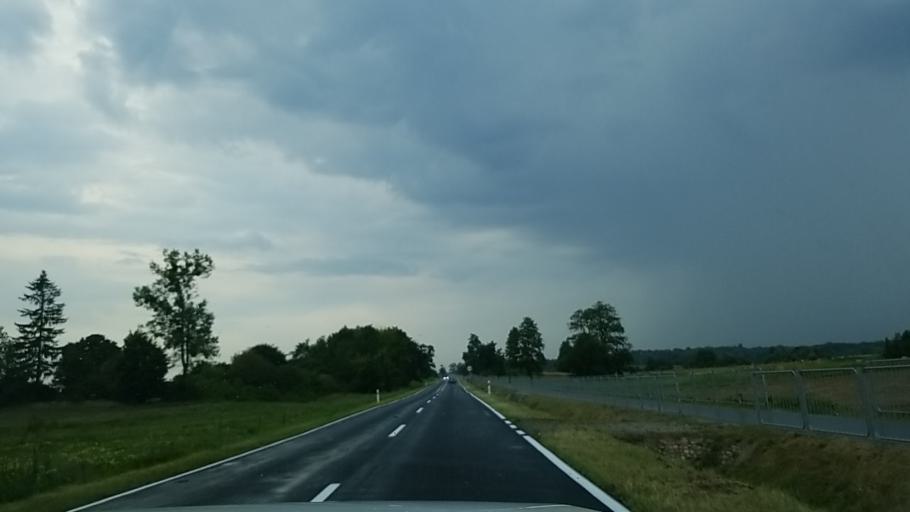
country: PL
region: Lublin Voivodeship
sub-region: Powiat wlodawski
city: Wlodawa
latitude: 51.5955
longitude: 23.5359
